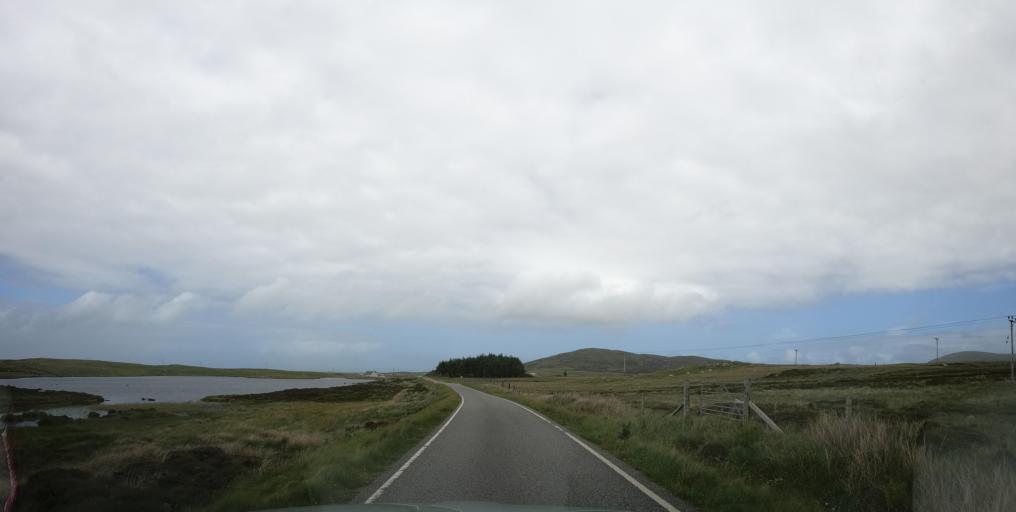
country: GB
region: Scotland
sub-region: Eilean Siar
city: Isle of South Uist
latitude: 57.2832
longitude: -7.3661
